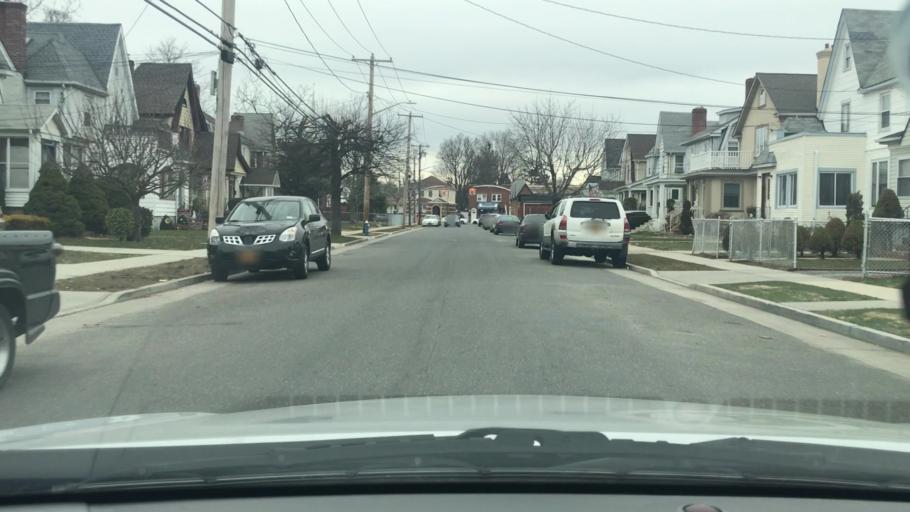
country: US
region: New York
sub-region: Nassau County
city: Uniondale
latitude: 40.7008
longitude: -73.6022
